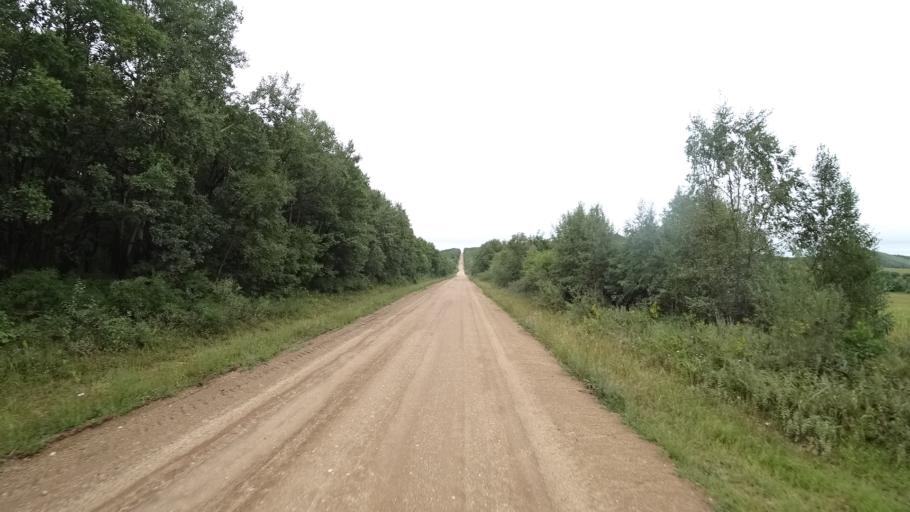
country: RU
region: Primorskiy
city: Ivanovka
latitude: 44.0212
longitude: 132.5206
